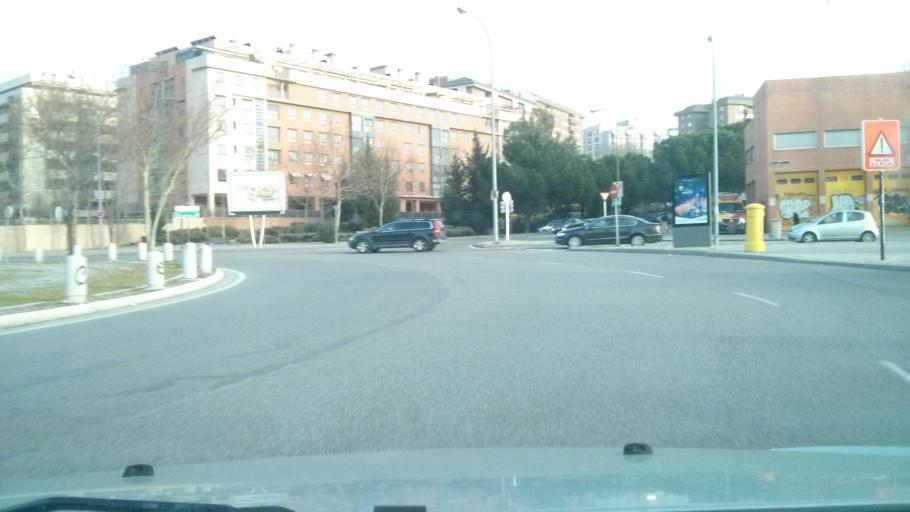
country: ES
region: Madrid
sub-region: Provincia de Madrid
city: Tetuan de las Victorias
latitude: 40.4756
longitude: -3.7219
